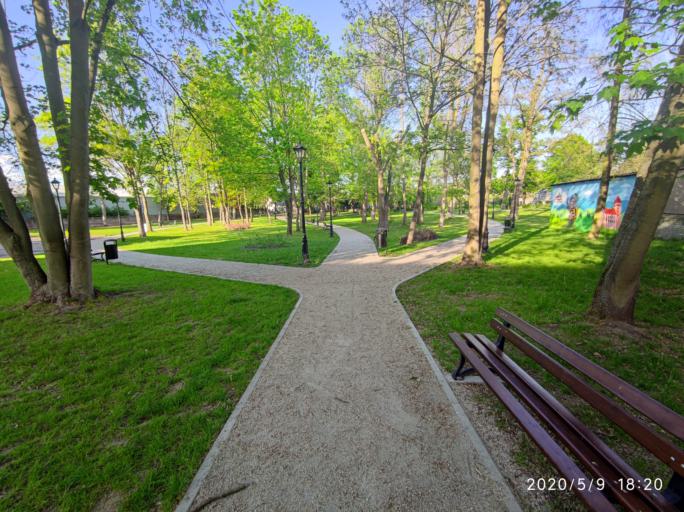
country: PL
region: Lubusz
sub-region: Powiat zielonogorski
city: Sulechow
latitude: 52.0866
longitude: 15.6282
